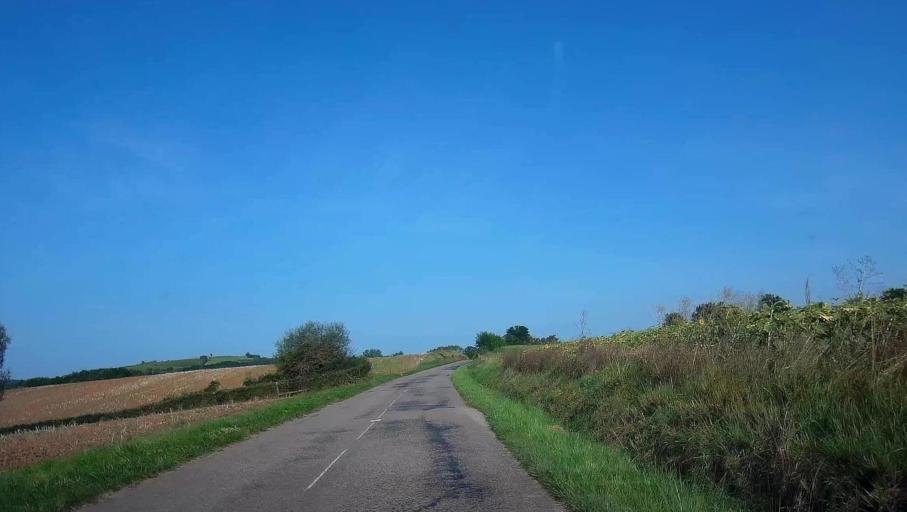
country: FR
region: Bourgogne
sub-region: Departement de Saone-et-Loire
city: Saint-Leger-sur-Dheune
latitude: 46.8707
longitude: 4.6127
